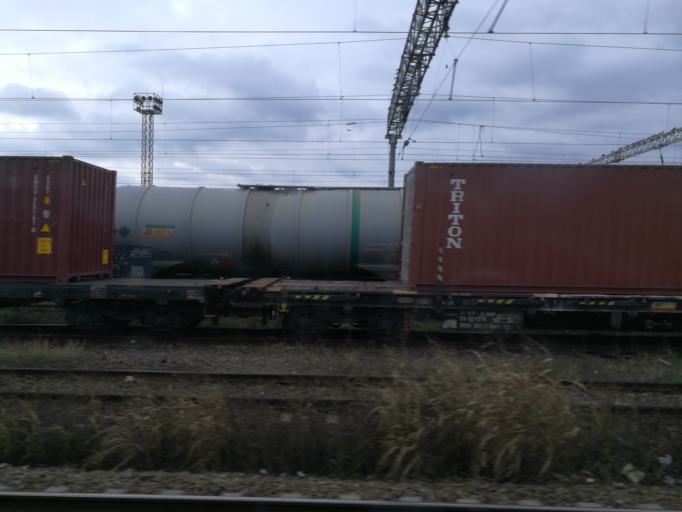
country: RO
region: Bacau
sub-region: Municipiul Bacau
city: Bacau
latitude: 46.5629
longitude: 26.8975
